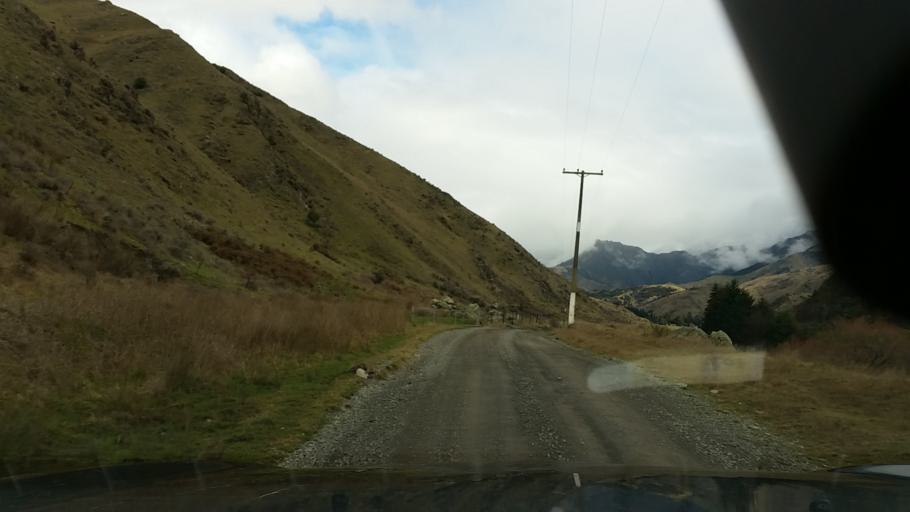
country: NZ
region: Tasman
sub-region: Tasman District
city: Richmond
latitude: -41.7297
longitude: 173.4434
